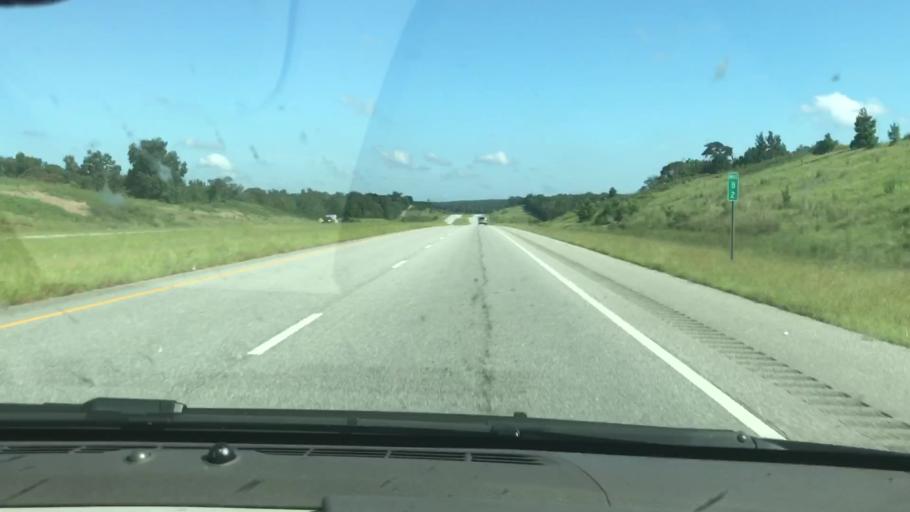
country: US
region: Alabama
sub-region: Barbour County
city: Eufaula
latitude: 32.0964
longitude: -85.1499
